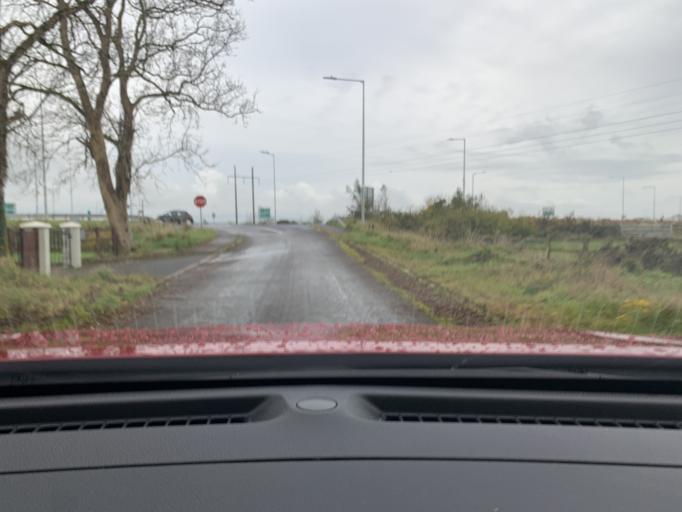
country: IE
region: Connaught
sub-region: Roscommon
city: Ballaghaderreen
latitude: 53.9136
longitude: -8.5542
